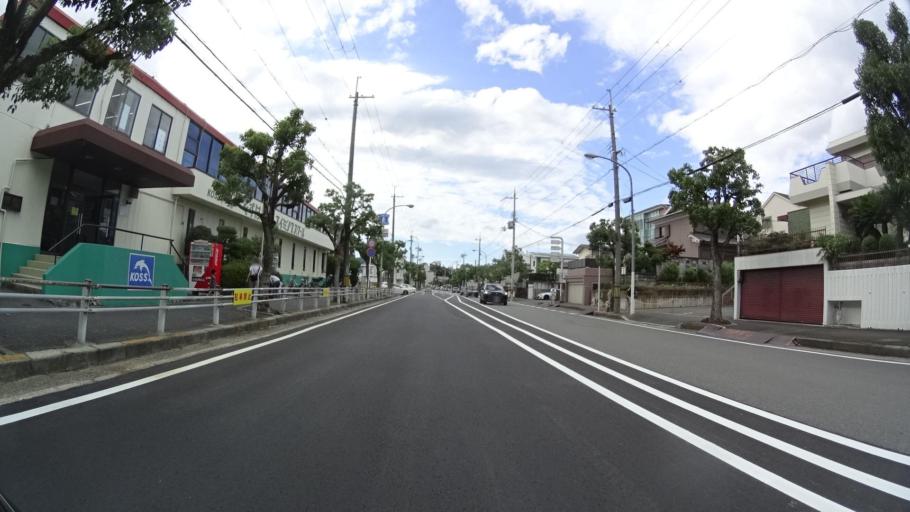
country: JP
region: Kyoto
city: Yawata
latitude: 34.8668
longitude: 135.6925
